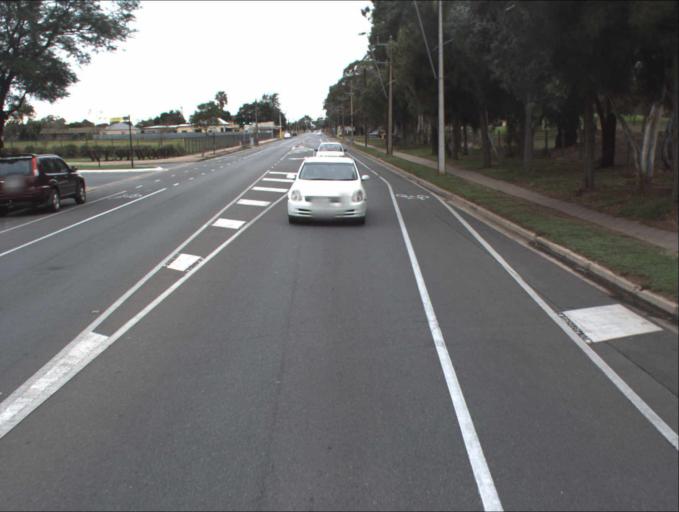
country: AU
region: South Australia
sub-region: Charles Sturt
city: Woodville
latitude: -34.8680
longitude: 138.5658
